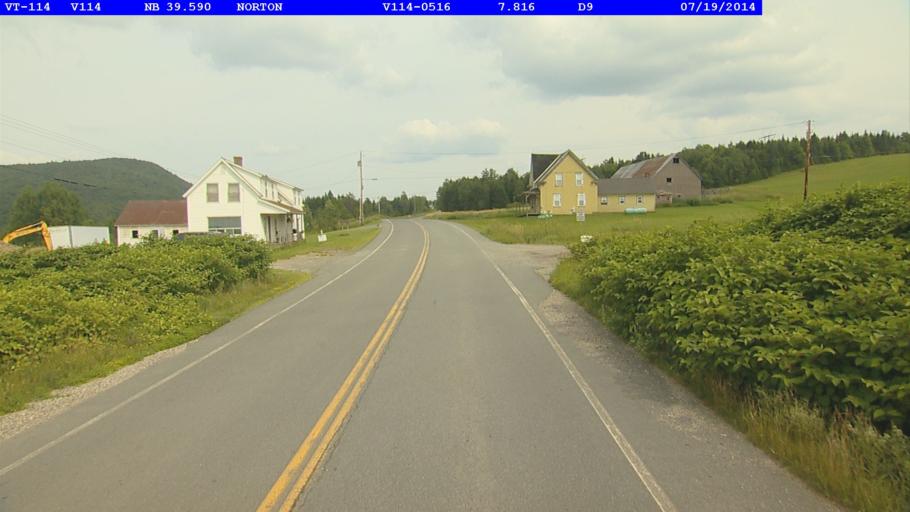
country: CA
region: Quebec
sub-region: Estrie
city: Coaticook
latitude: 44.9988
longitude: -71.7488
